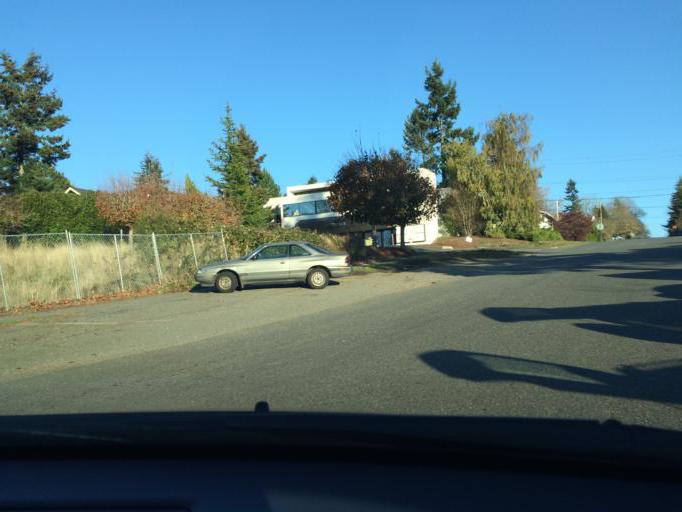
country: US
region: Washington
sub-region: Whatcom County
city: Bellingham
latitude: 48.7210
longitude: -122.5021
